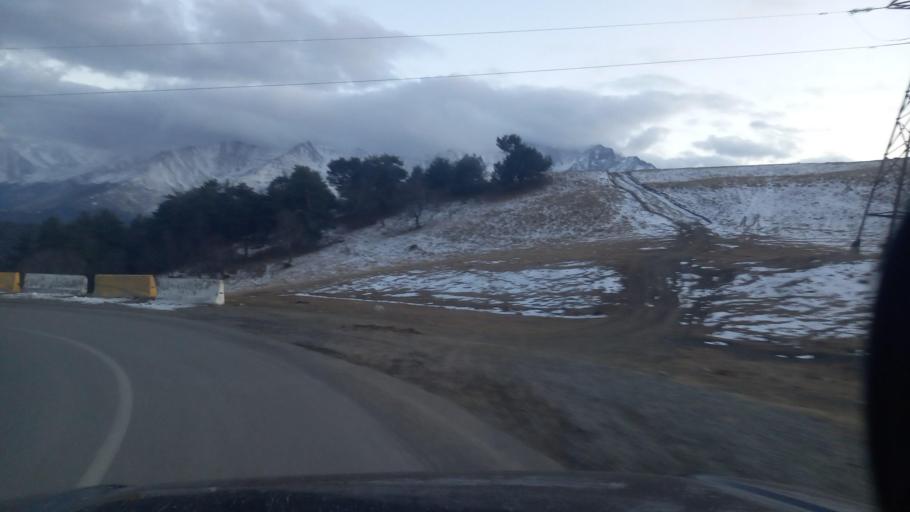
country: RU
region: Ingushetiya
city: Dzhayrakh
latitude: 42.8182
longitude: 44.8393
